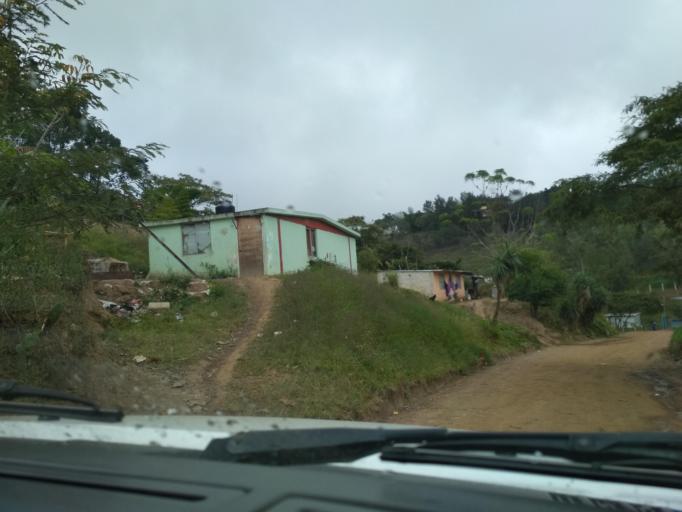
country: MX
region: Veracruz
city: El Castillo
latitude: 19.5414
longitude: -96.8328
